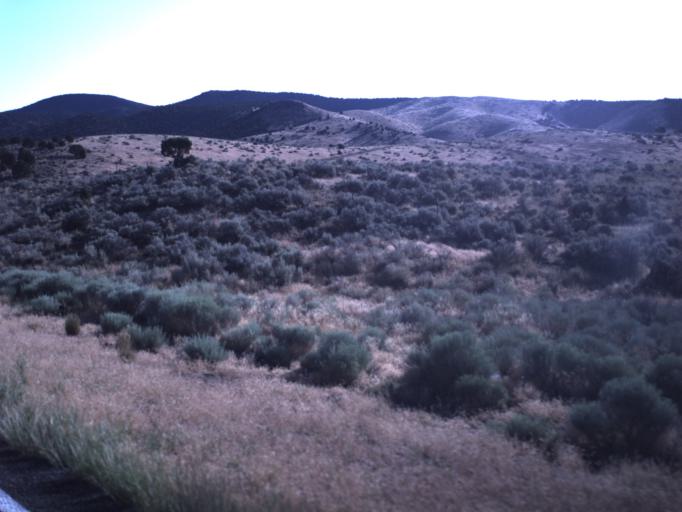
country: US
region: Utah
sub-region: Iron County
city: Parowan
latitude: 38.0978
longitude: -112.9497
